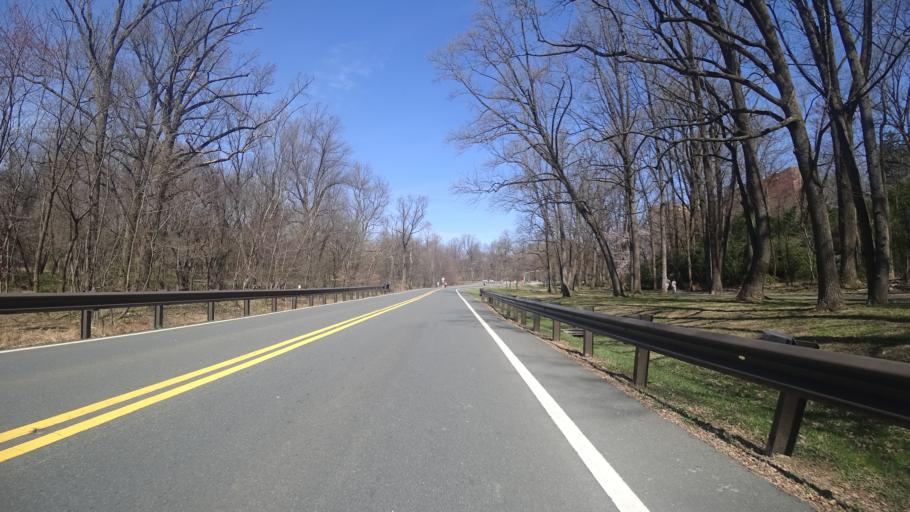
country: US
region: Maryland
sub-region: Montgomery County
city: Kemp Mill
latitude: 39.0351
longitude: -77.0300
